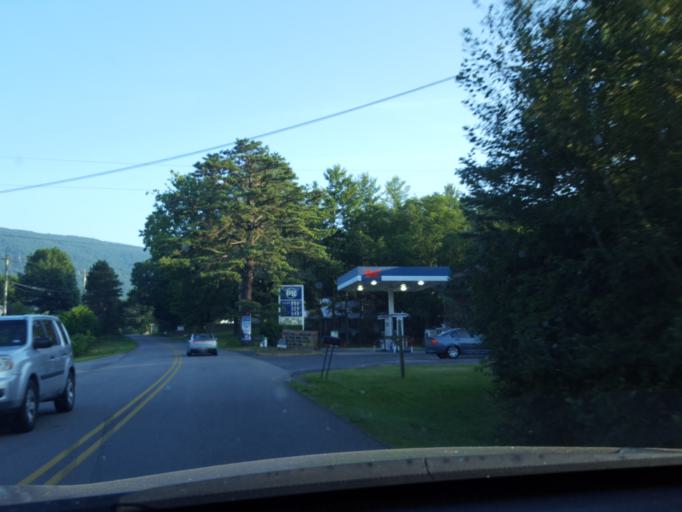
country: US
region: Virginia
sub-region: Augusta County
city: Lyndhurst
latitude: 37.9615
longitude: -78.9620
